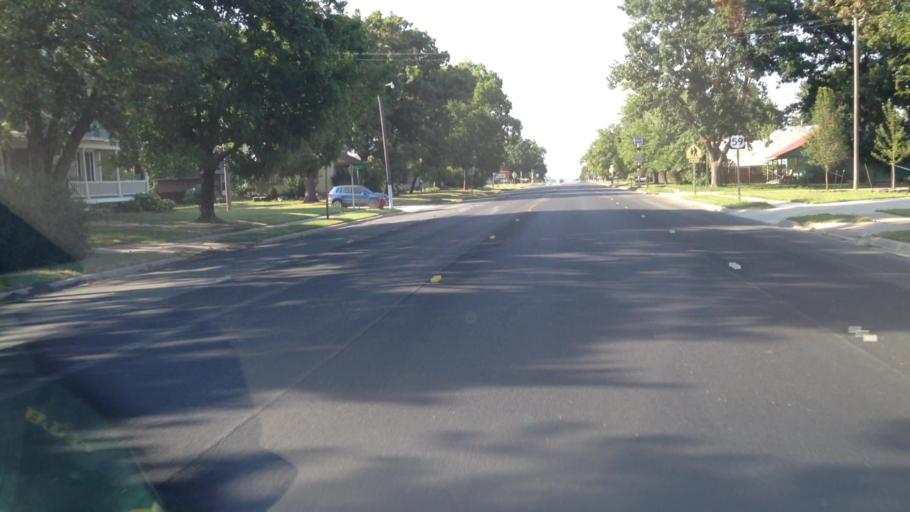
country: US
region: Kansas
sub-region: Allen County
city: Iola
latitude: 37.9171
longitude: -95.1701
